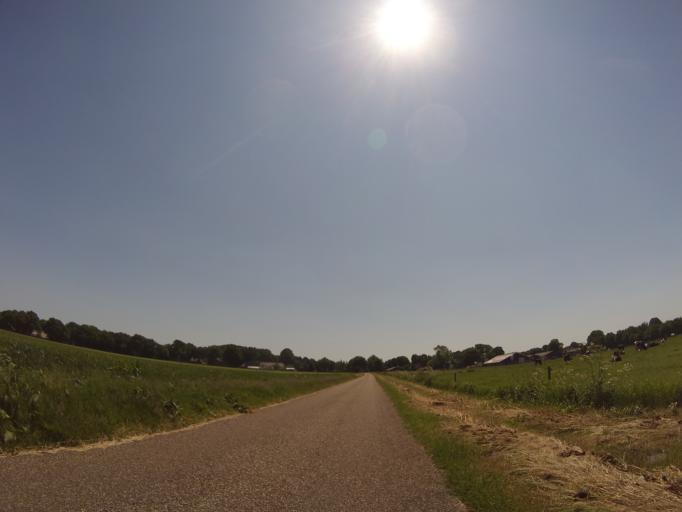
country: NL
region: Drenthe
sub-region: Gemeente Coevorden
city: Sleen
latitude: 52.7590
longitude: 6.8231
